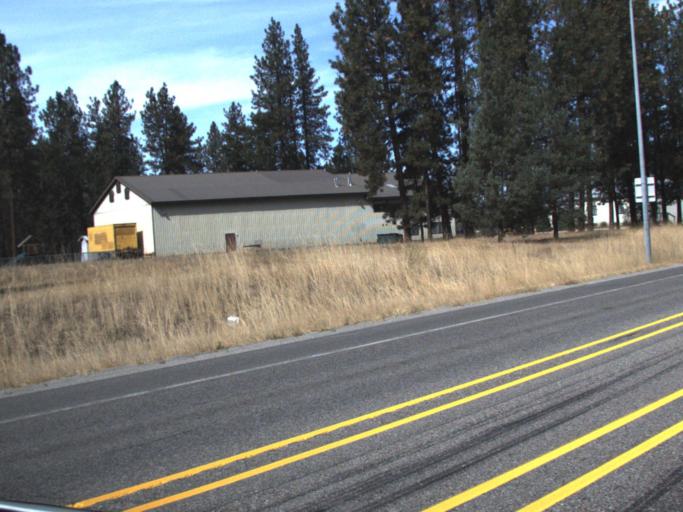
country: US
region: Washington
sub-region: Stevens County
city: Chewelah
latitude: 48.1564
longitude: -117.6919
